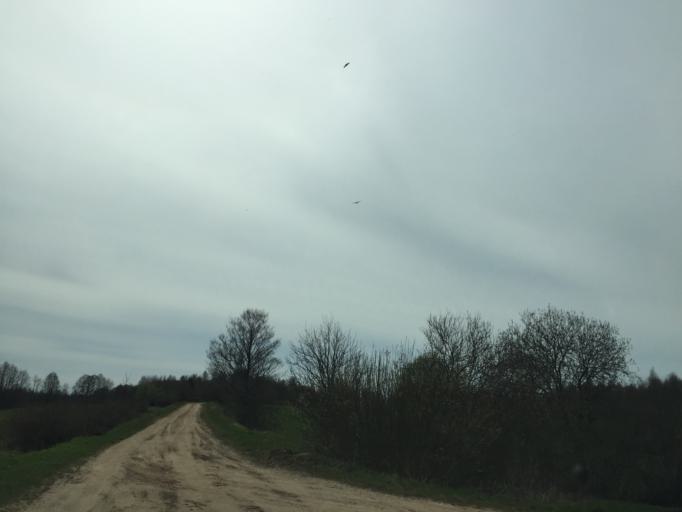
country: LV
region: Ludzas Rajons
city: Ludza
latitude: 56.5257
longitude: 27.5823
